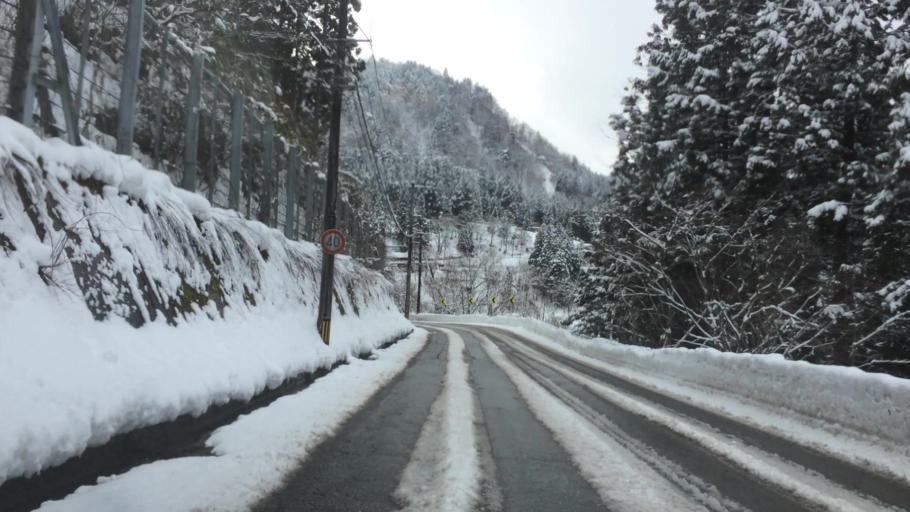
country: JP
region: Toyama
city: Kamiichi
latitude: 36.5706
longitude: 137.3662
